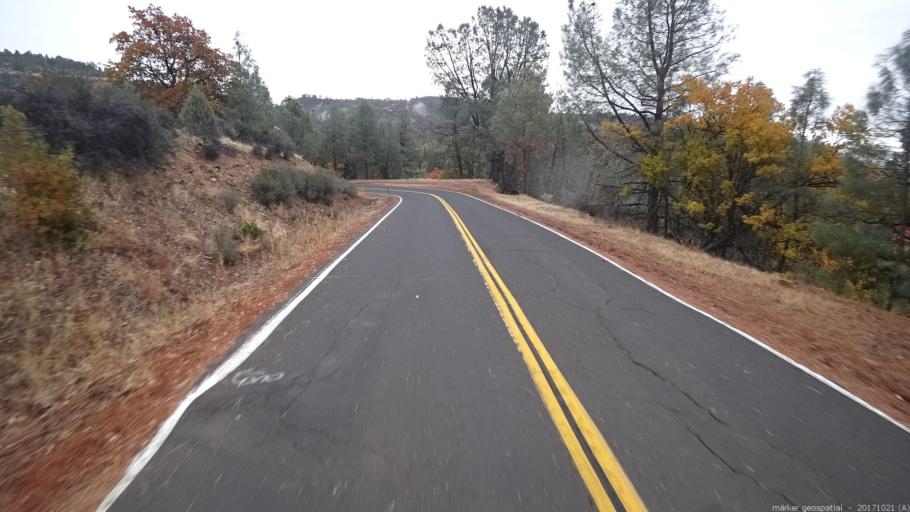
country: US
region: California
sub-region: Shasta County
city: Burney
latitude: 40.9943
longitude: -121.5036
